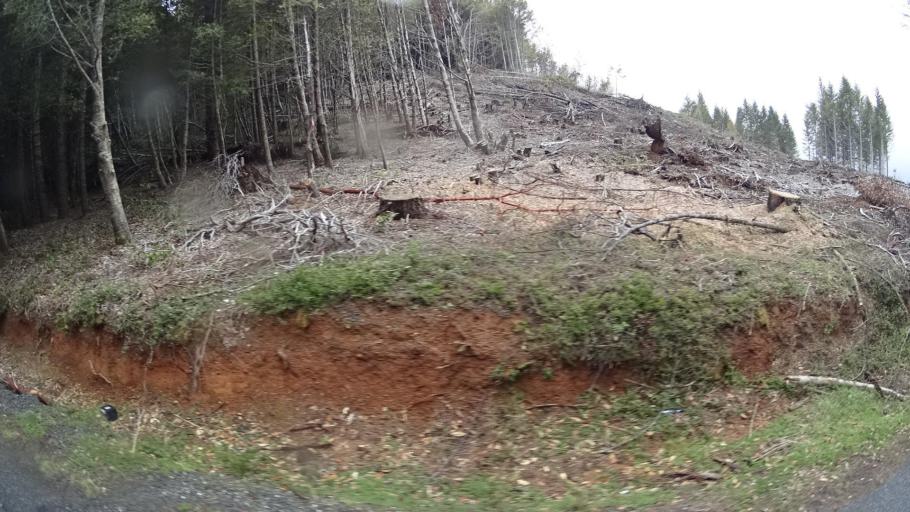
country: US
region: California
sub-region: Humboldt County
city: Willow Creek
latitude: 41.2011
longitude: -123.7915
